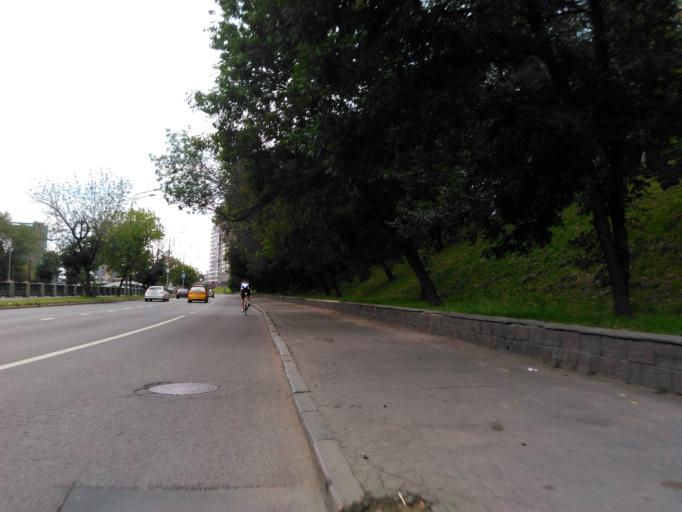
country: RU
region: Moscow
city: Lefortovo
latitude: 55.7883
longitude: 37.6986
